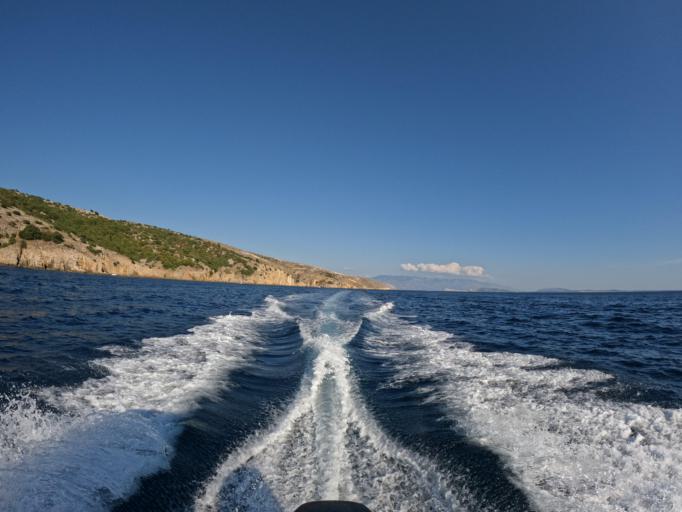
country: HR
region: Primorsko-Goranska
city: Punat
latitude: 44.9747
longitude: 14.6246
